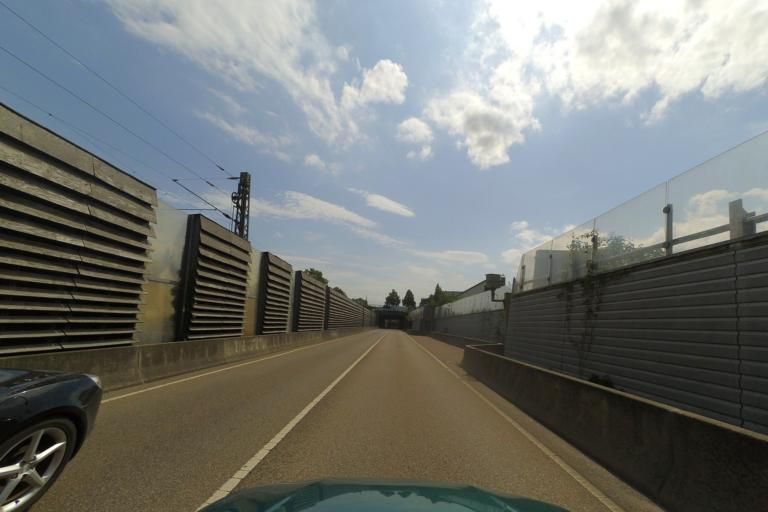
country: DE
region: Baden-Wuerttemberg
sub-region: Regierungsbezirk Stuttgart
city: Huttlingen
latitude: 48.8642
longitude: 10.1064
